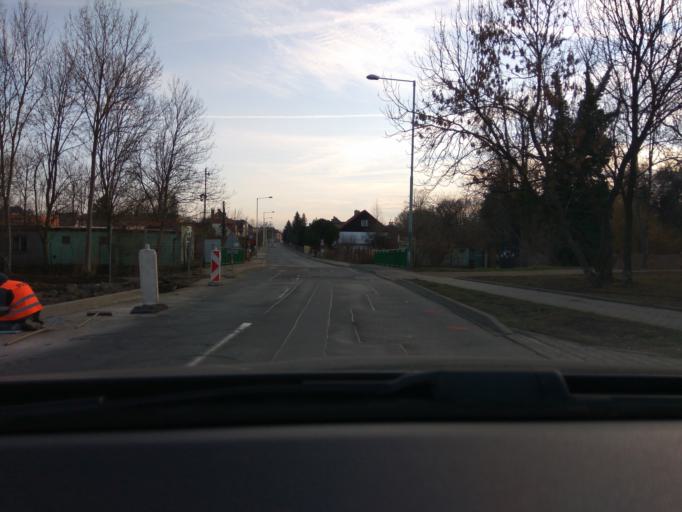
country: CZ
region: Praha
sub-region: Praha 18
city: Letnany
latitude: 50.1557
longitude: 14.5224
